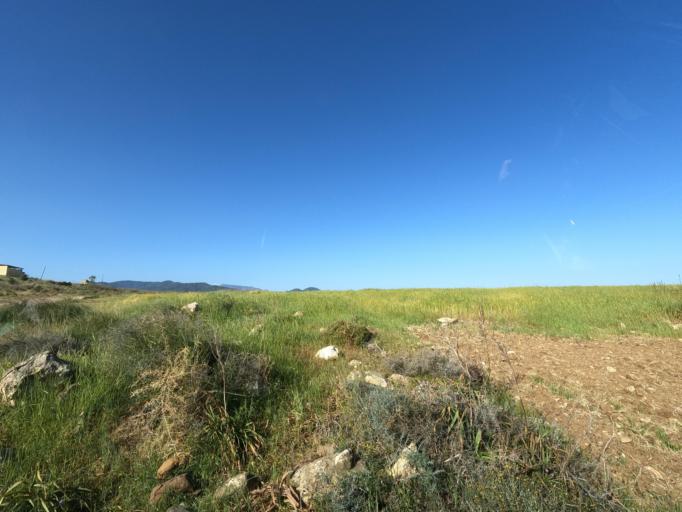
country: CY
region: Lefkosia
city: Astromeritis
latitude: 35.0828
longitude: 33.0250
